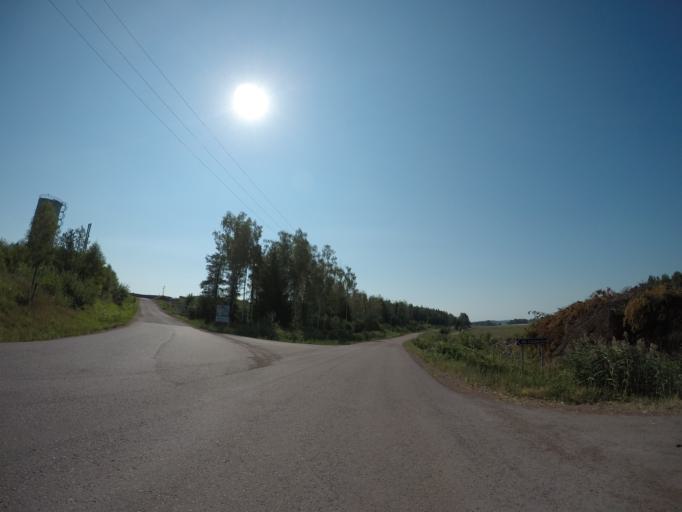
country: AX
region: Alands landsbygd
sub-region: Saltvik
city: Saltvik
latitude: 60.2280
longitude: 20.0091
